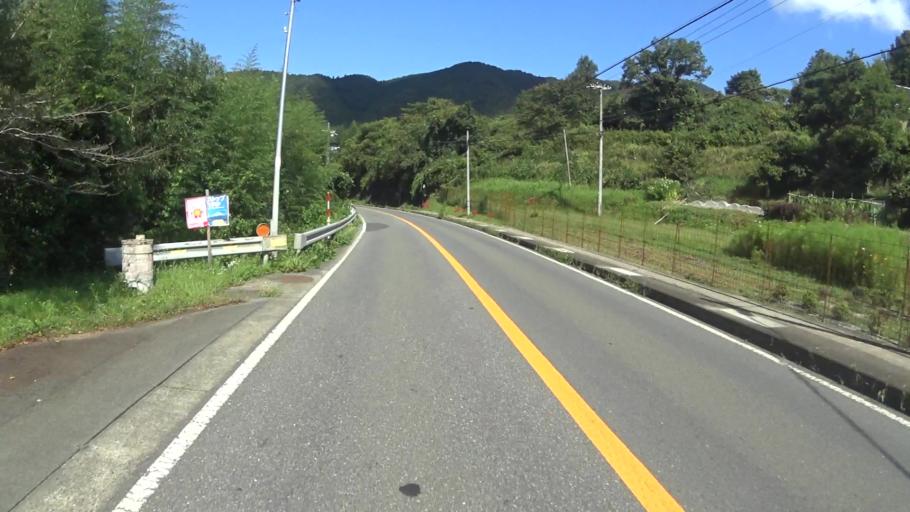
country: JP
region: Kyoto
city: Ayabe
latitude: 35.2959
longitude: 135.3288
